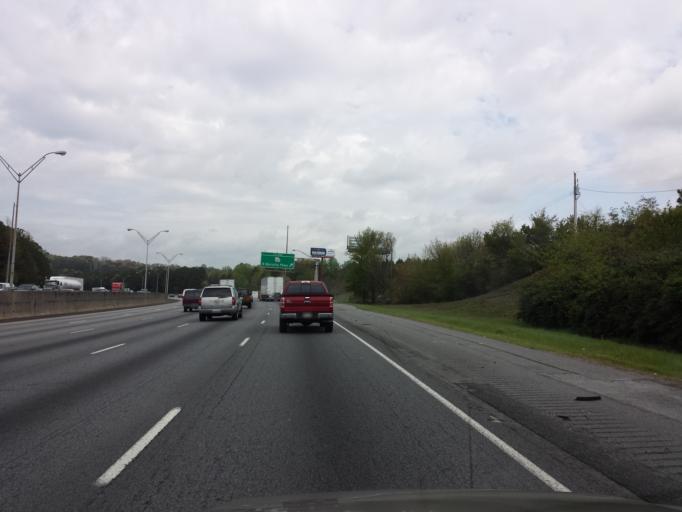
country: US
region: Georgia
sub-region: Cobb County
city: Marietta
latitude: 33.9557
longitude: -84.5162
